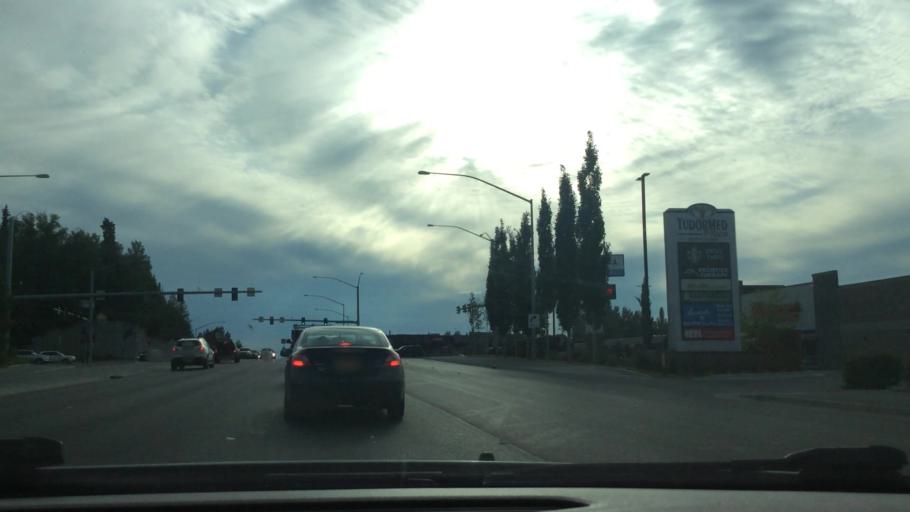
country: US
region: Alaska
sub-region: Anchorage Municipality
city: Anchorage
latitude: 61.1811
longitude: -149.8359
